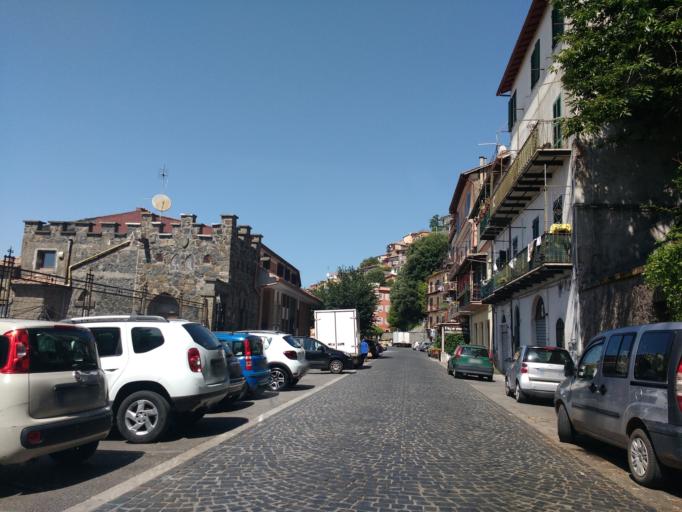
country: IT
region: Latium
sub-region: Citta metropolitana di Roma Capitale
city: Rocca di Papa
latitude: 41.7586
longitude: 12.7080
